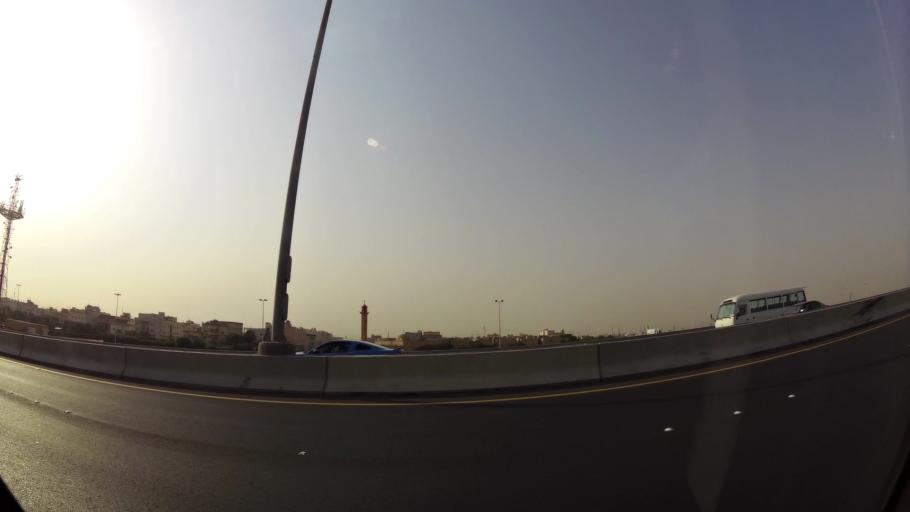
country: KW
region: Al Asimah
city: Ar Rabiyah
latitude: 29.3106
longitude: 47.8673
